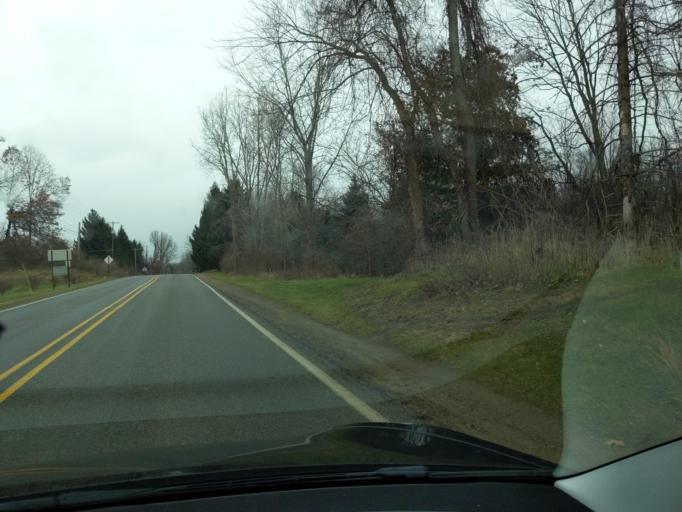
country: US
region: Michigan
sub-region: Jackson County
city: Spring Arbor
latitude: 42.2468
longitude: -84.5373
